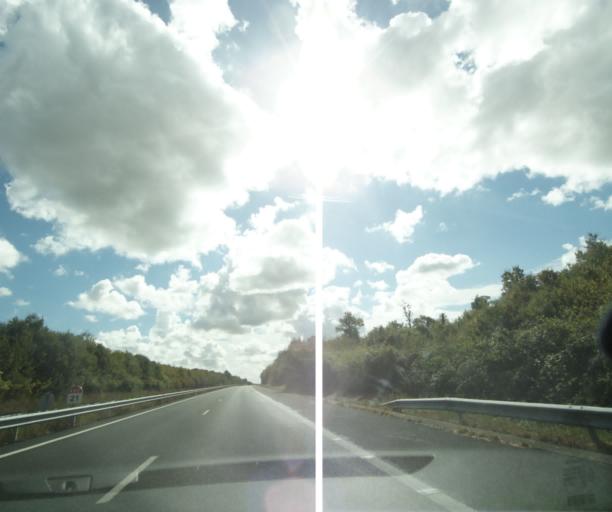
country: FR
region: Poitou-Charentes
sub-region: Departement de la Charente-Maritime
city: Bords
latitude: 45.9032
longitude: -0.7648
